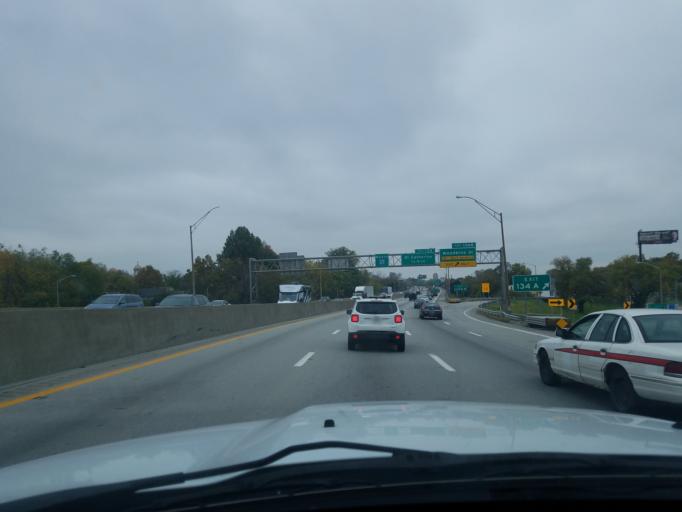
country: US
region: Kentucky
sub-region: Jefferson County
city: Louisville
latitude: 38.2267
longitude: -85.7516
